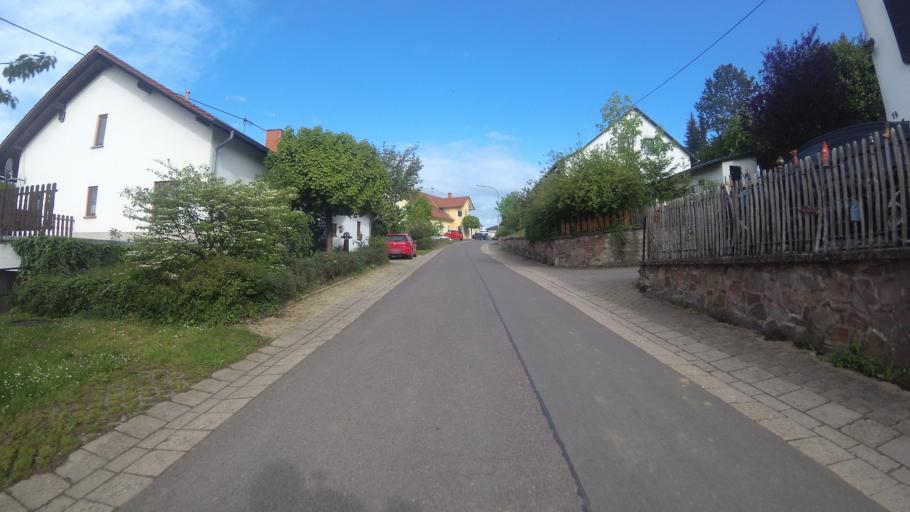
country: DE
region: Saarland
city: Merzig
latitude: 49.4244
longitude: 6.5682
